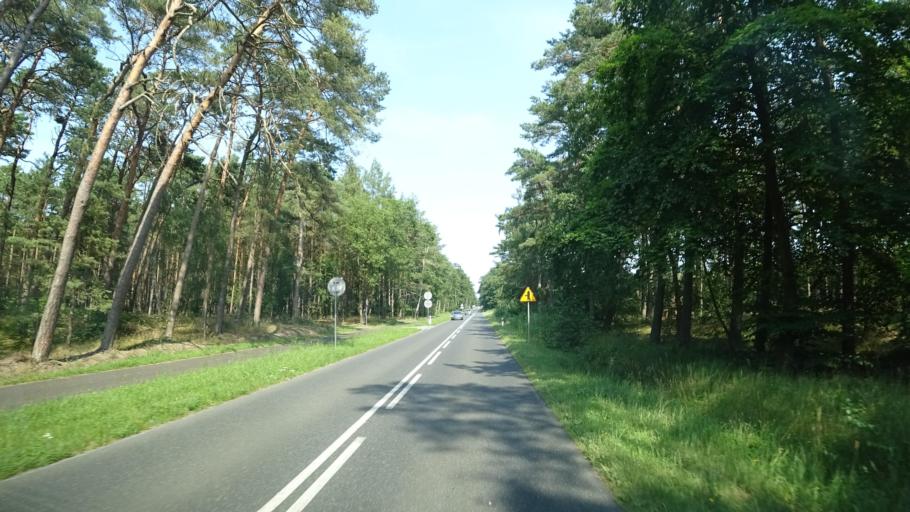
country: PL
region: West Pomeranian Voivodeship
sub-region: Powiat kamienski
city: Dziwnow
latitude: 53.9968
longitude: 14.6643
